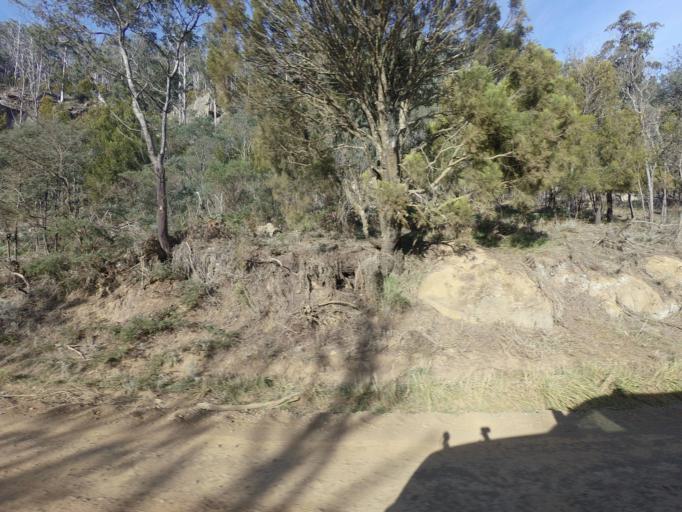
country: AU
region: Tasmania
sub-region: Sorell
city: Sorell
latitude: -42.4962
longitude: 147.4333
